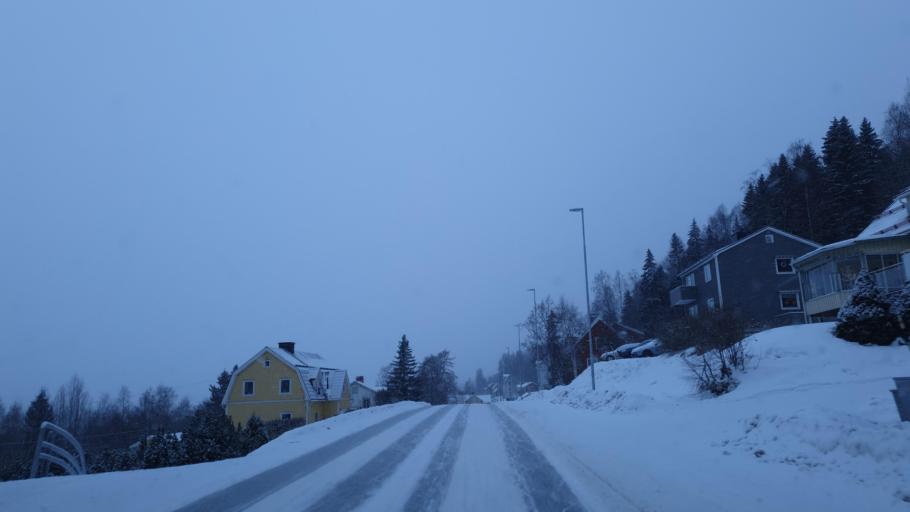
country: SE
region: Vaesternorrland
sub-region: OErnskoeldsviks Kommun
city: Ornskoldsvik
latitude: 63.2982
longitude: 18.6644
